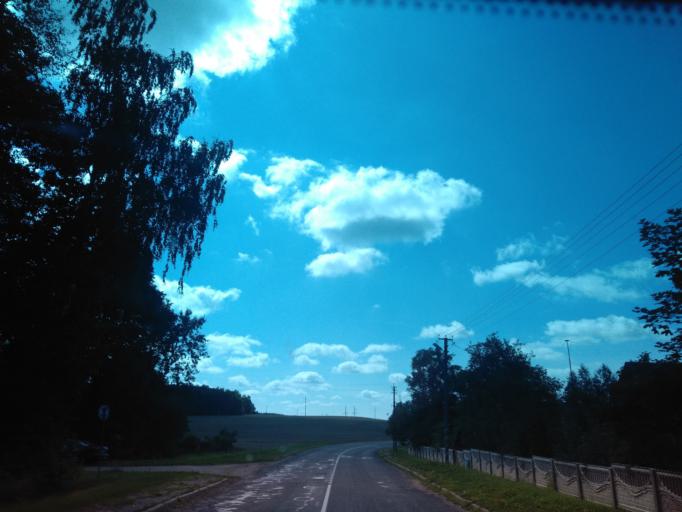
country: BY
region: Minsk
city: Uzda
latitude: 53.3867
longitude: 27.2430
